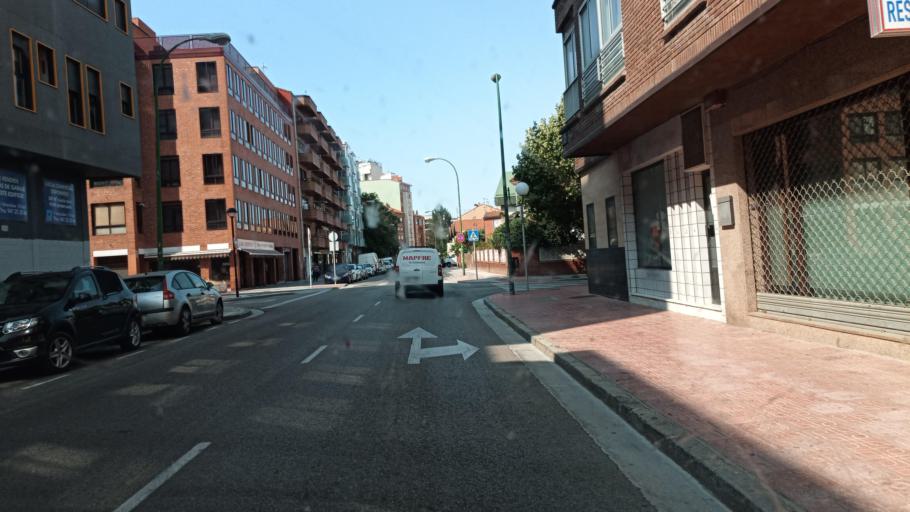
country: ES
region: Castille and Leon
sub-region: Provincia de Burgos
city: Burgos
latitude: 42.3389
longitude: -3.6896
